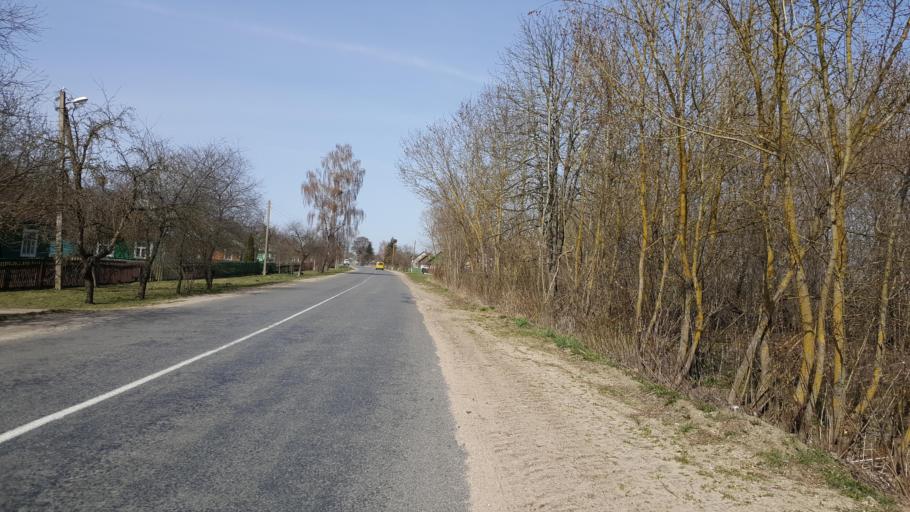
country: BY
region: Brest
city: Kamyanyets
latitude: 52.4247
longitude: 23.7705
